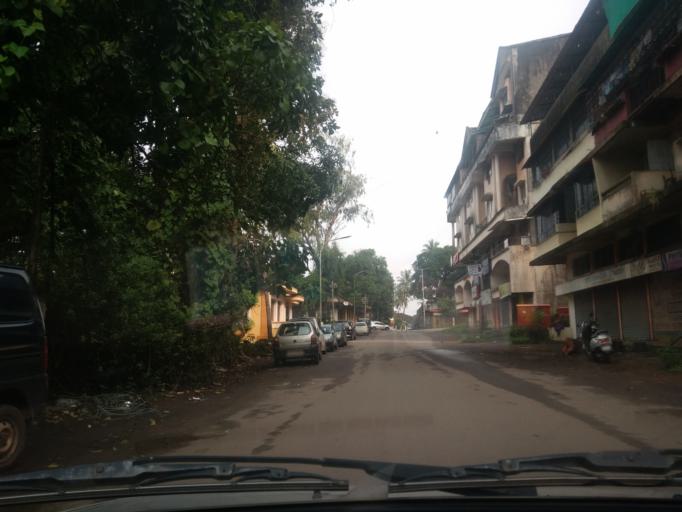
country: IN
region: Goa
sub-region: South Goa
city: Madgaon
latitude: 15.2739
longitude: 73.9550
